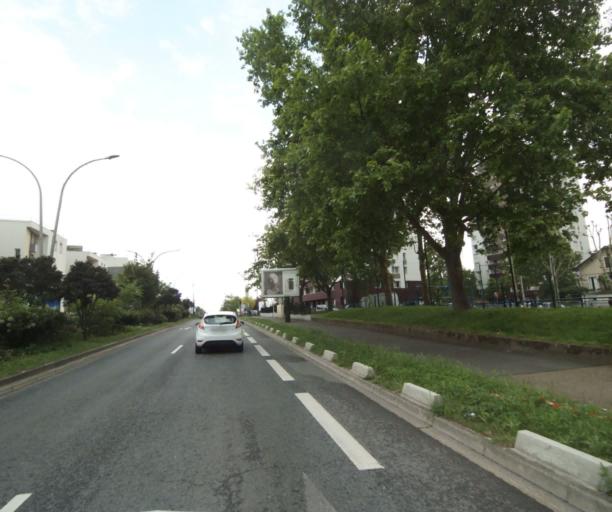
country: FR
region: Ile-de-France
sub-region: Departement du Val-d'Oise
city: Argenteuil
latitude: 48.9478
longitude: 2.2379
